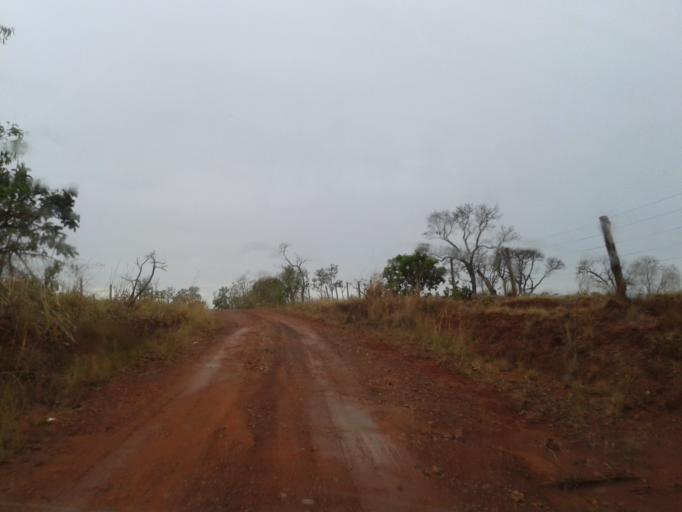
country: BR
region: Minas Gerais
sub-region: Campina Verde
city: Campina Verde
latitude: -19.3168
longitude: -49.5098
